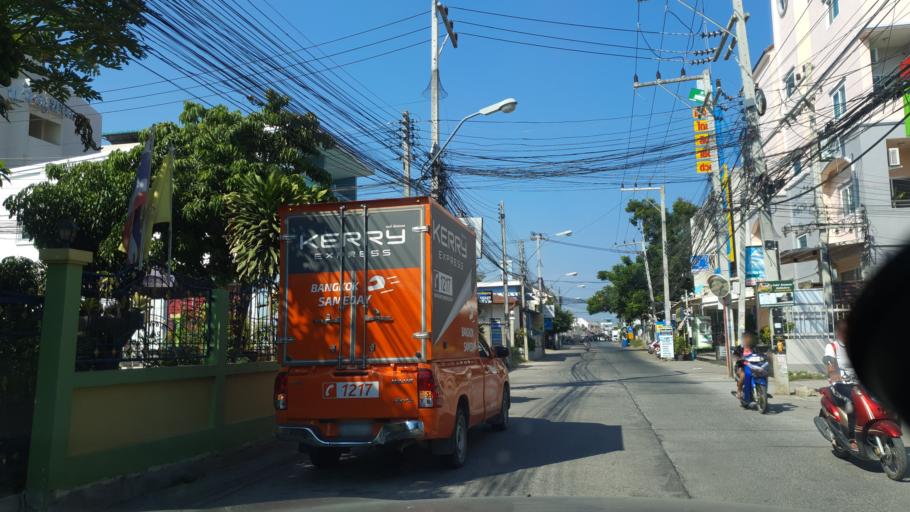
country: TH
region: Prachuap Khiri Khan
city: Hua Hin
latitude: 12.5556
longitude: 99.9526
